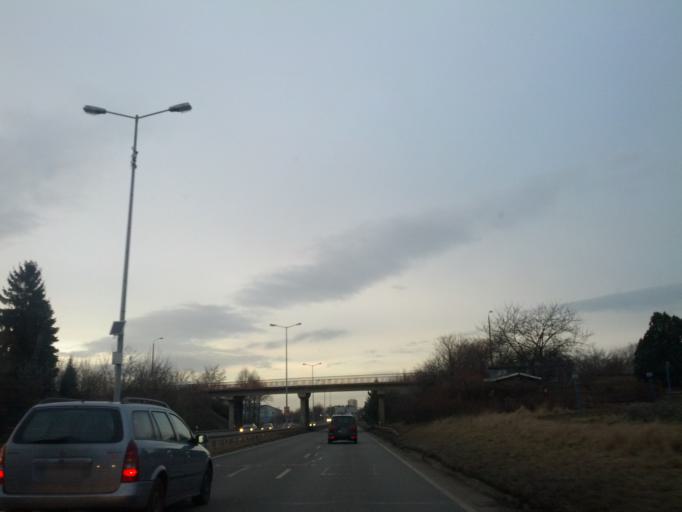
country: DE
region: Thuringia
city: Erfurt
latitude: 50.9891
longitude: 11.0046
